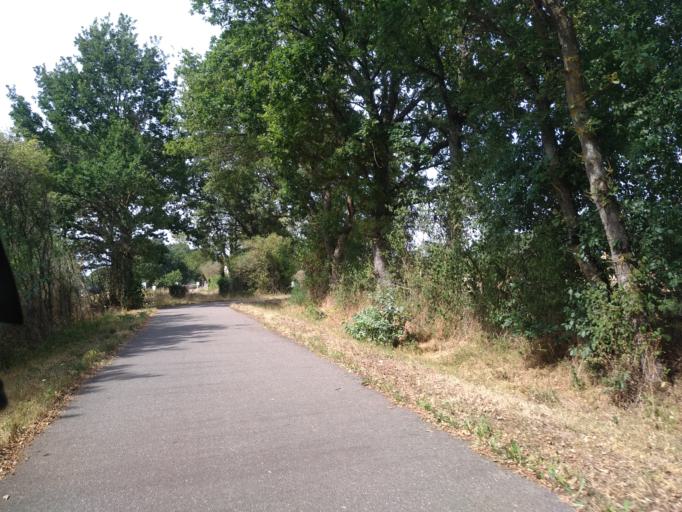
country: FR
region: Bourgogne
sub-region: Departement de Saone-et-Loire
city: Bourbon-Lancy
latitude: 46.5926
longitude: 3.7457
